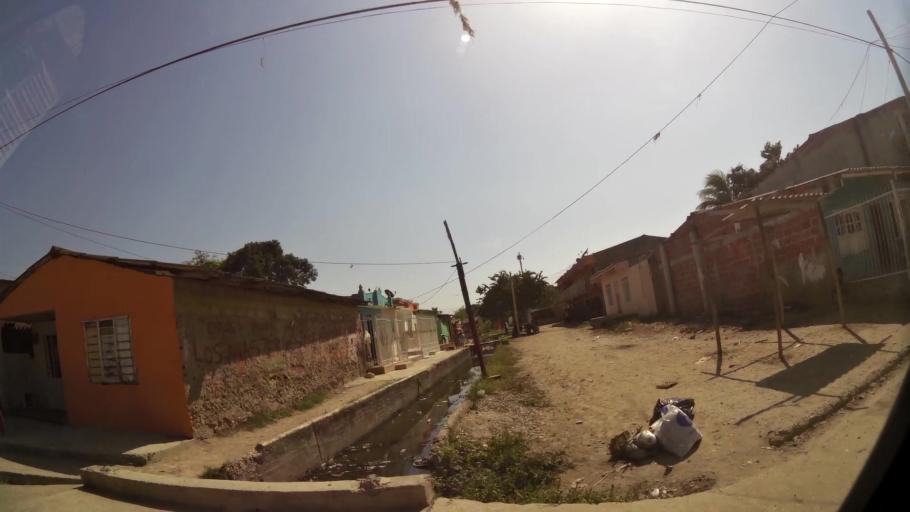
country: CO
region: Bolivar
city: Cartagena
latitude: 10.4128
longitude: -75.5156
